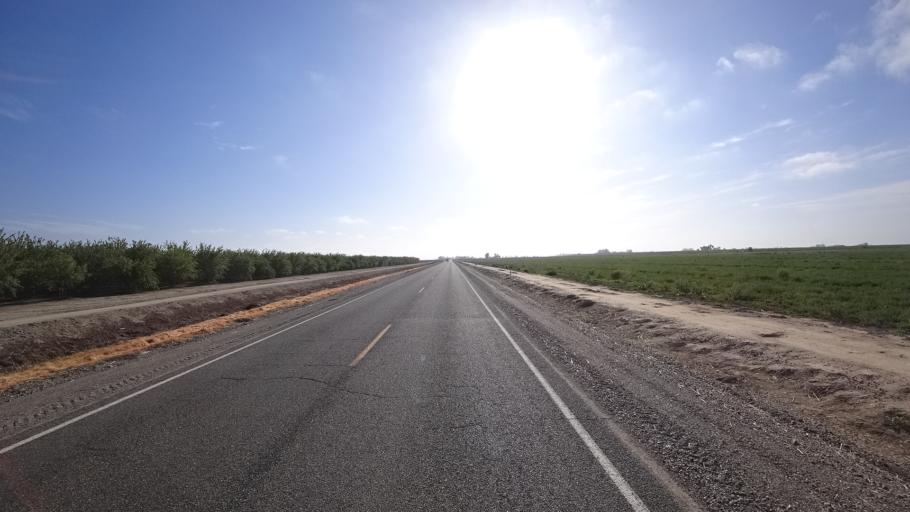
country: US
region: California
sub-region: Glenn County
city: Willows
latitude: 39.5822
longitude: -122.1328
